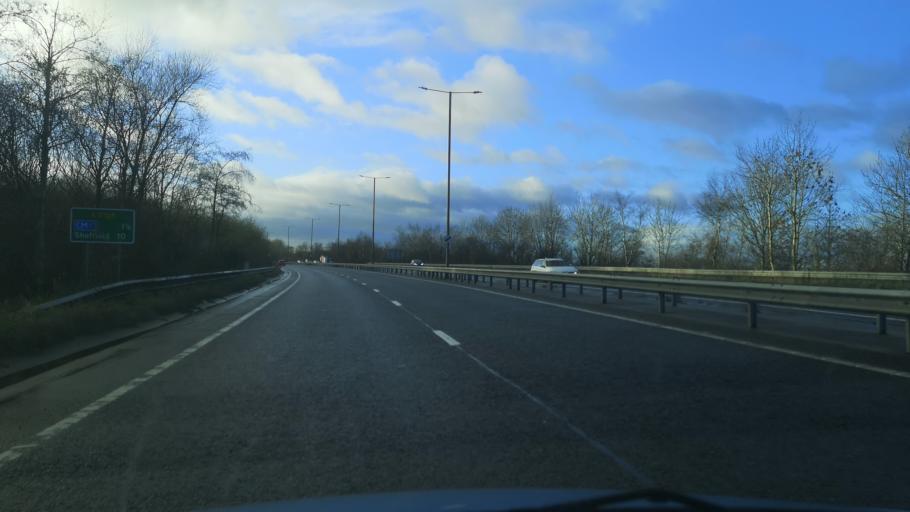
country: GB
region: England
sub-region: Barnsley
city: Hoyland Nether
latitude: 53.5095
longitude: -1.4494
